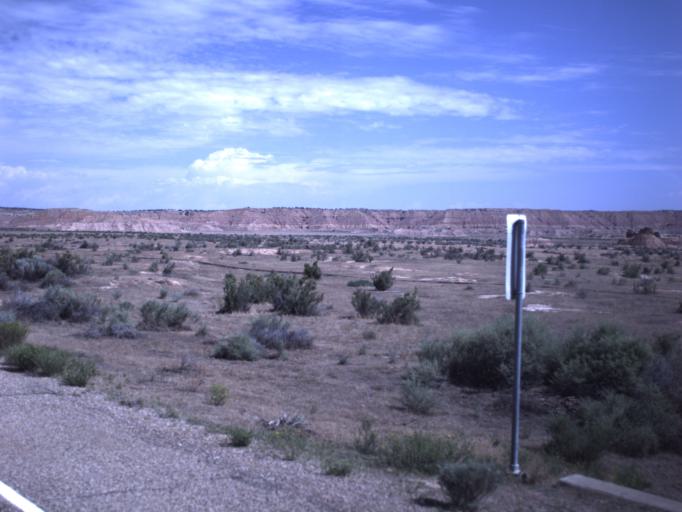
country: US
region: Utah
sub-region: Uintah County
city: Naples
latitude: 40.1296
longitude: -109.2626
